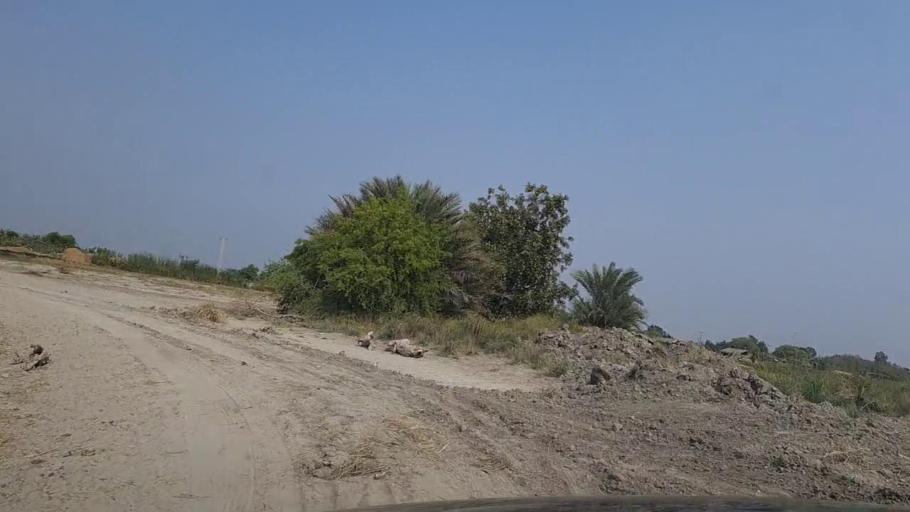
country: PK
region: Sindh
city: Thatta
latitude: 24.7554
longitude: 67.7994
